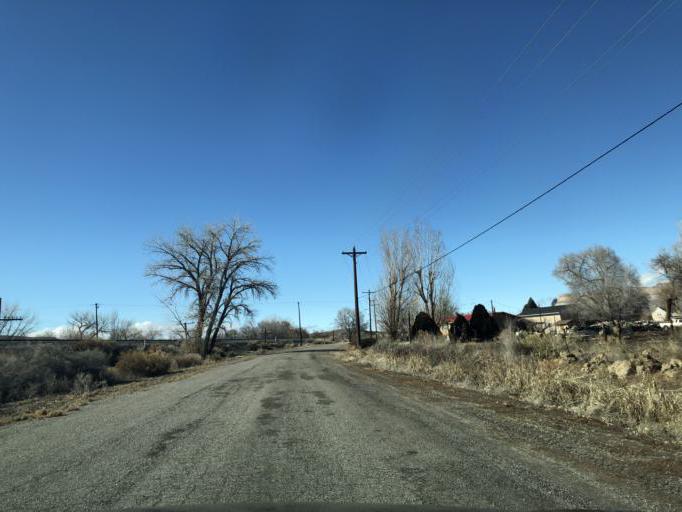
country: US
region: Utah
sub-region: Carbon County
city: East Carbon City
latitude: 38.9865
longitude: -110.1559
